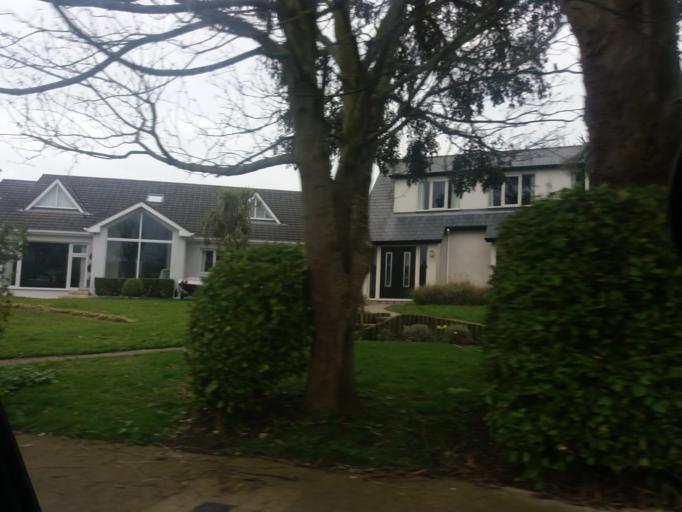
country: IE
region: Leinster
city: Sutton
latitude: 53.3877
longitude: -6.0961
